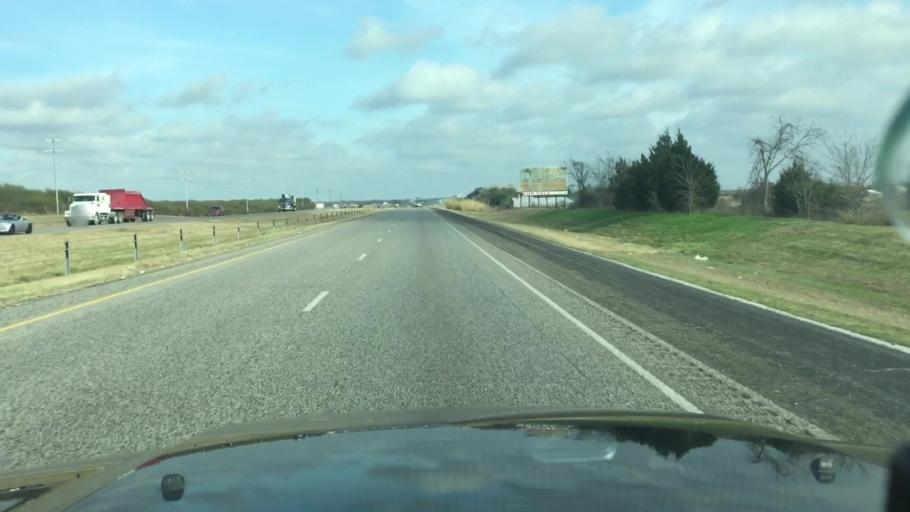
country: US
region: Texas
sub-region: Washington County
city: Brenham
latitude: 30.1379
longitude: -96.3219
